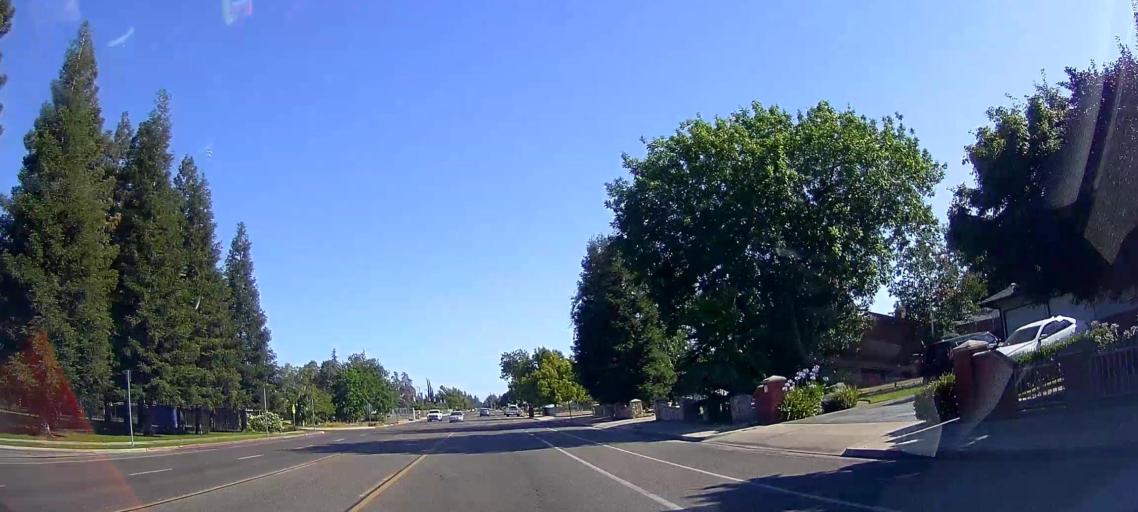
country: US
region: California
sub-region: Fresno County
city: Fresno
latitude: 36.8198
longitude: -119.7994
